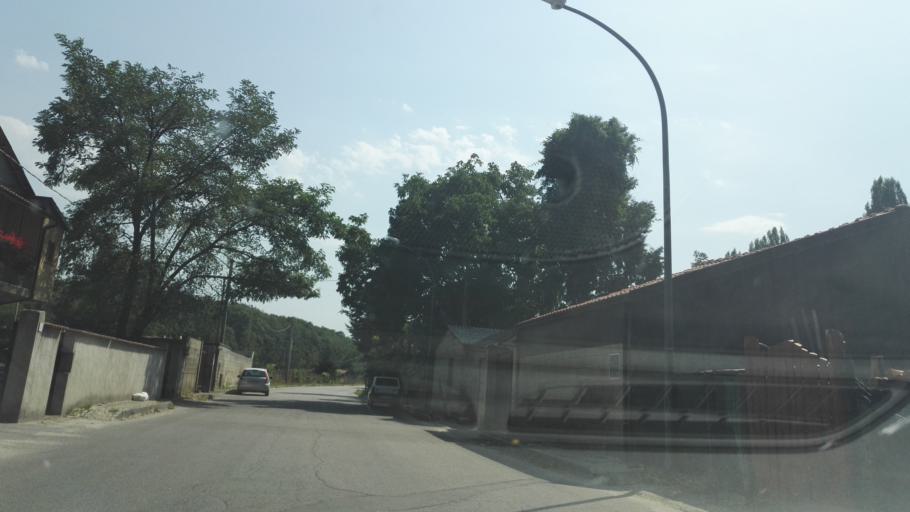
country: IT
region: Calabria
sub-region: Provincia di Vibo-Valentia
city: Serra San Bruno
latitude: 38.5755
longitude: 16.3319
